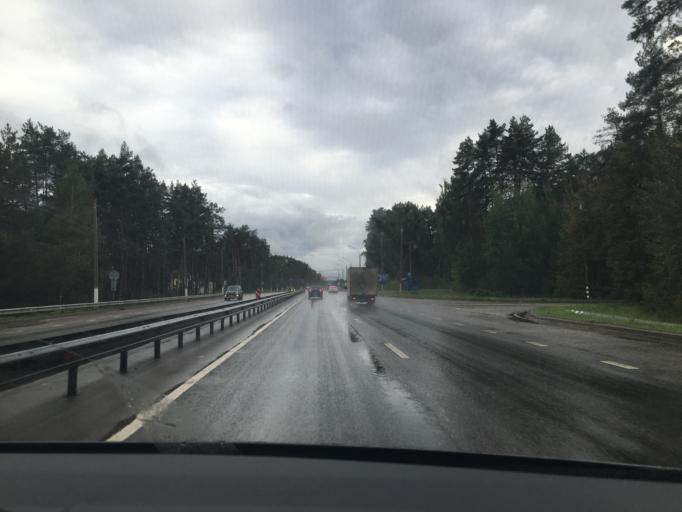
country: RU
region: Kaluga
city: Obninsk
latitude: 55.0602
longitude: 36.6206
